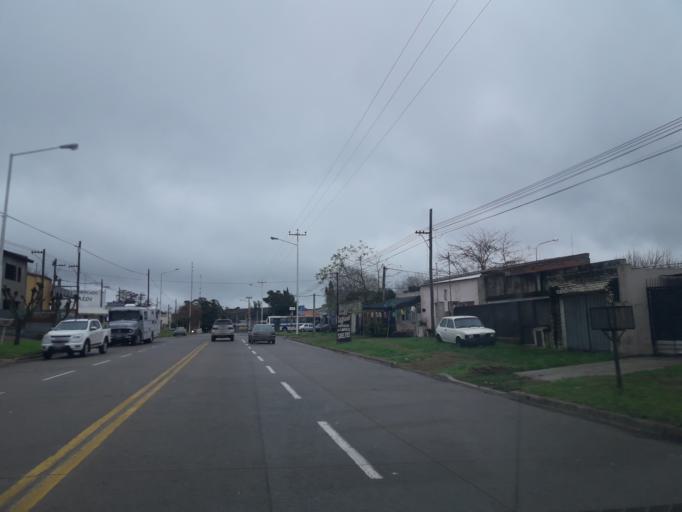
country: AR
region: Buenos Aires
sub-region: Partido de Tandil
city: Tandil
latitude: -37.3201
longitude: -59.1625
